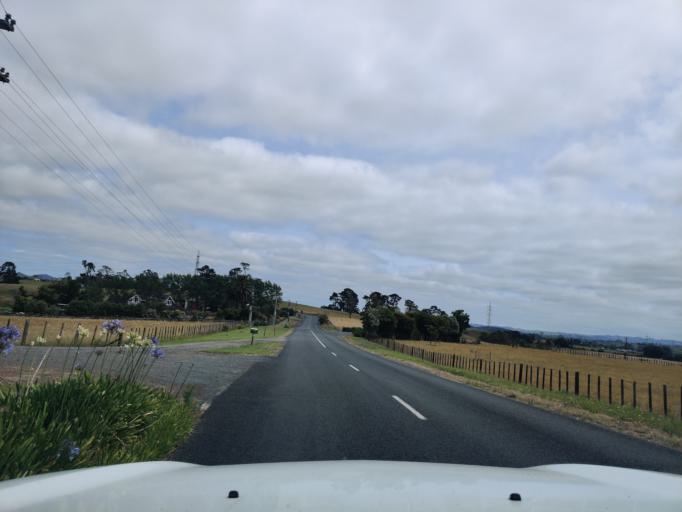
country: NZ
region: Waikato
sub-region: Waikato District
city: Te Kauwhata
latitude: -37.5116
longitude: 175.1770
